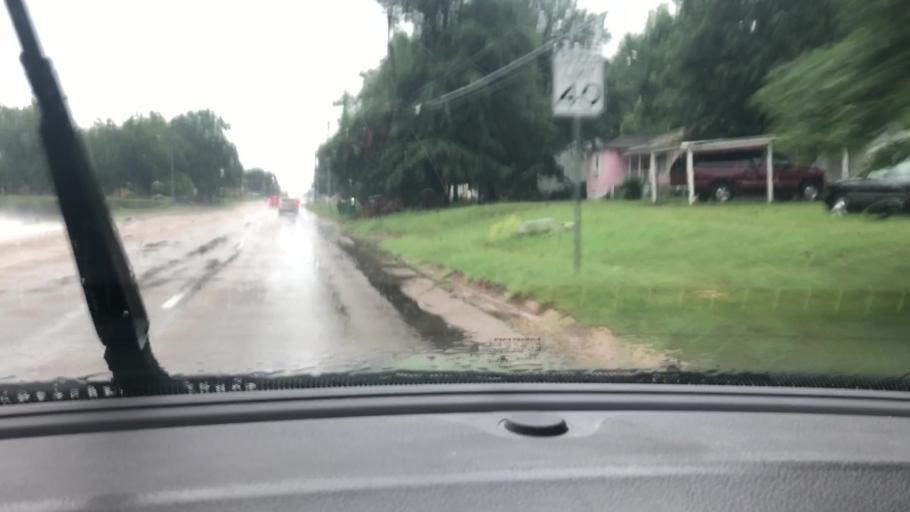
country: US
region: Texas
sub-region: Bowie County
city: Wake Village
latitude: 33.4435
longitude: -94.0804
